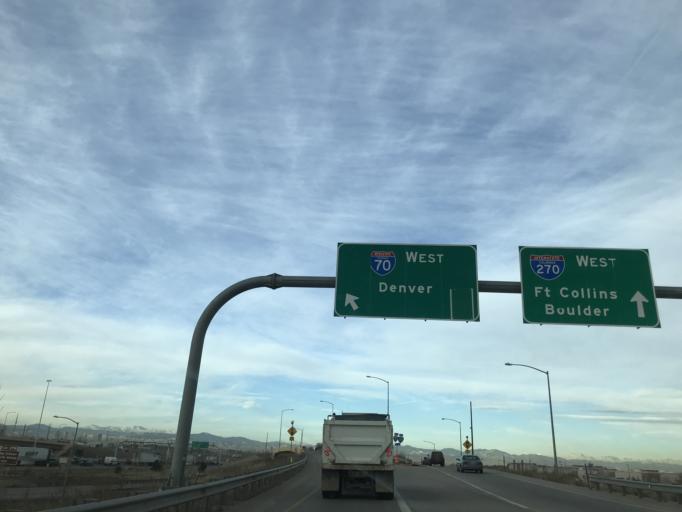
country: US
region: Colorado
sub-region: Adams County
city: Commerce City
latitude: 39.7783
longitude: -104.8847
